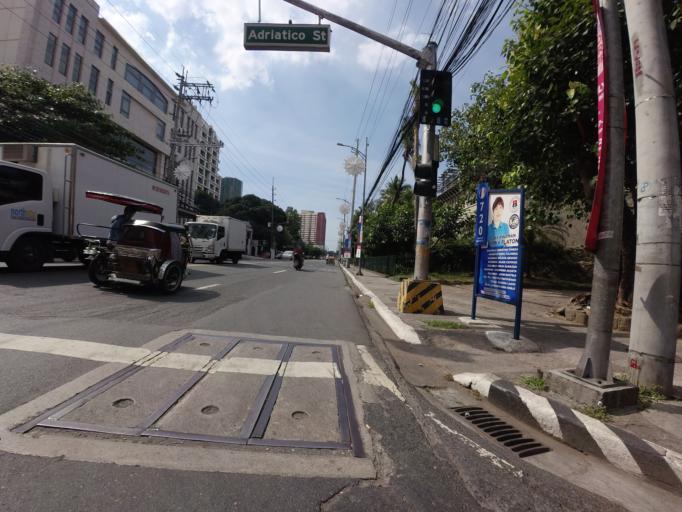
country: PH
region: Metro Manila
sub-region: City of Manila
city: Port Area
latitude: 14.5610
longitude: 120.9922
